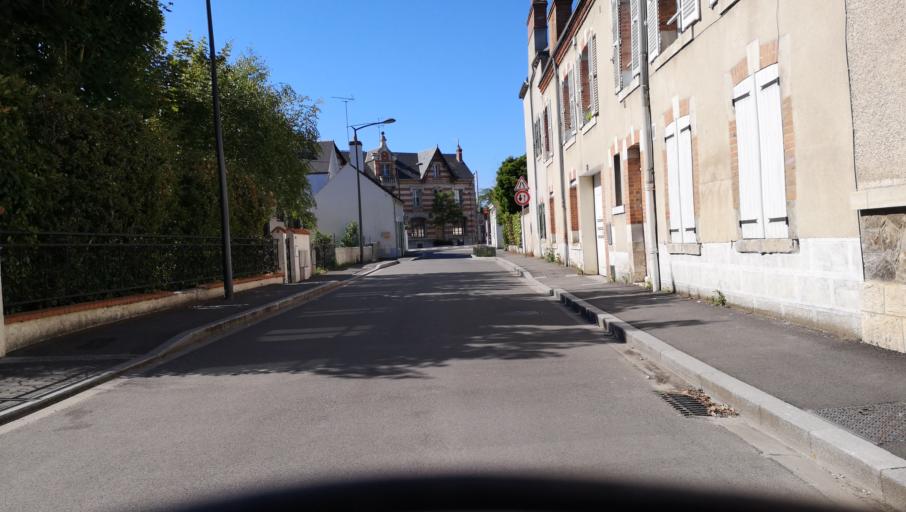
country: FR
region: Centre
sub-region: Departement du Loiret
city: Saint-Jean-le-Blanc
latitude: 47.9057
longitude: 1.9235
